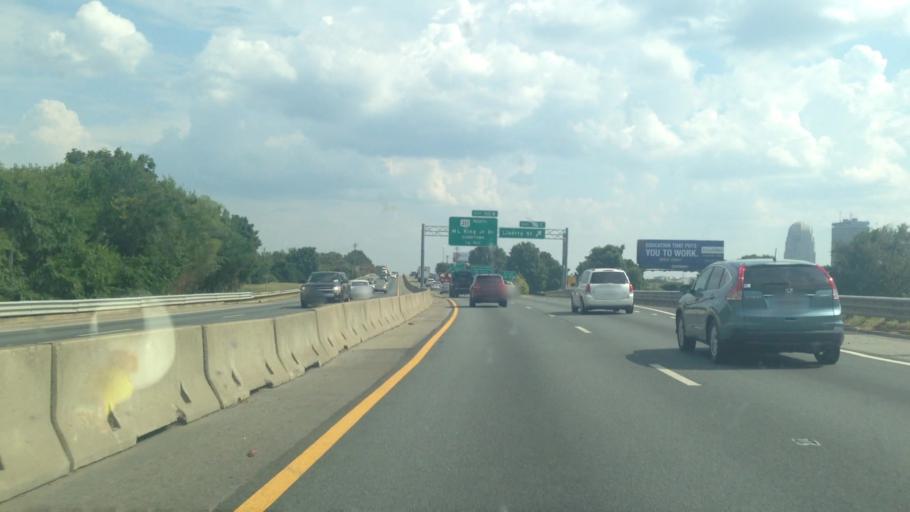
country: US
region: North Carolina
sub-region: Forsyth County
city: Winston-Salem
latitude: 36.1123
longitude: -80.2366
